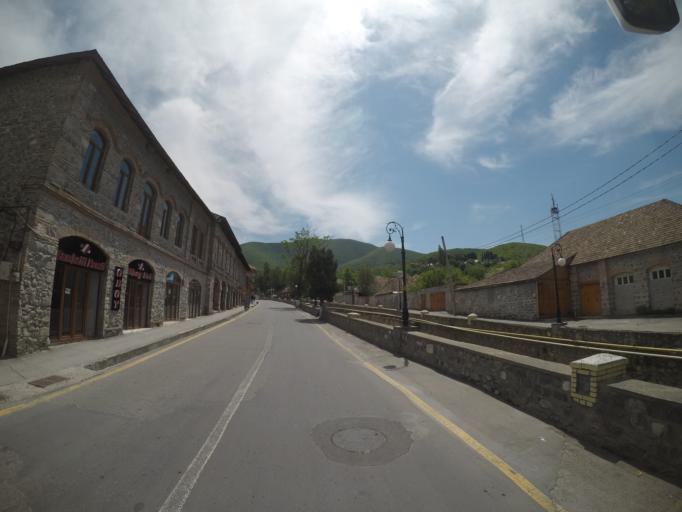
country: AZ
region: Shaki City
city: Sheki
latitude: 41.2017
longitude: 47.1824
